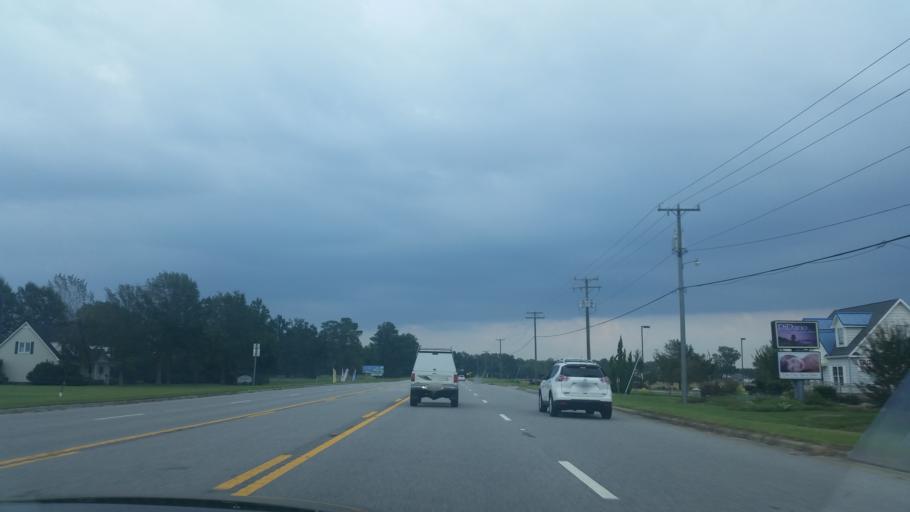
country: US
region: North Carolina
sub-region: Currituck County
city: Currituck
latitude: 36.4499
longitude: -76.0193
